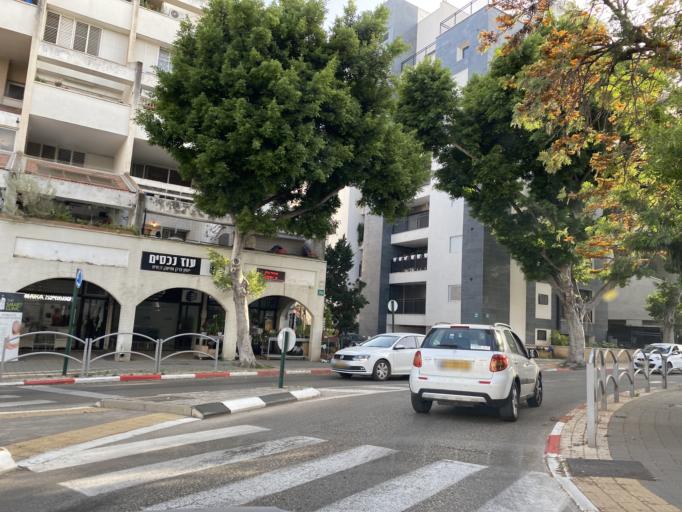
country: IL
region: Central District
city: Kfar Saba
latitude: 32.1783
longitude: 34.9090
